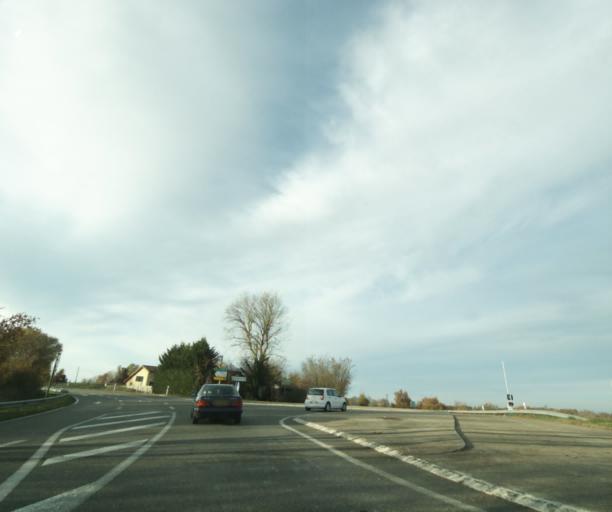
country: FR
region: Midi-Pyrenees
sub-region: Departement du Gers
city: Eauze
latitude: 43.7923
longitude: 0.1016
